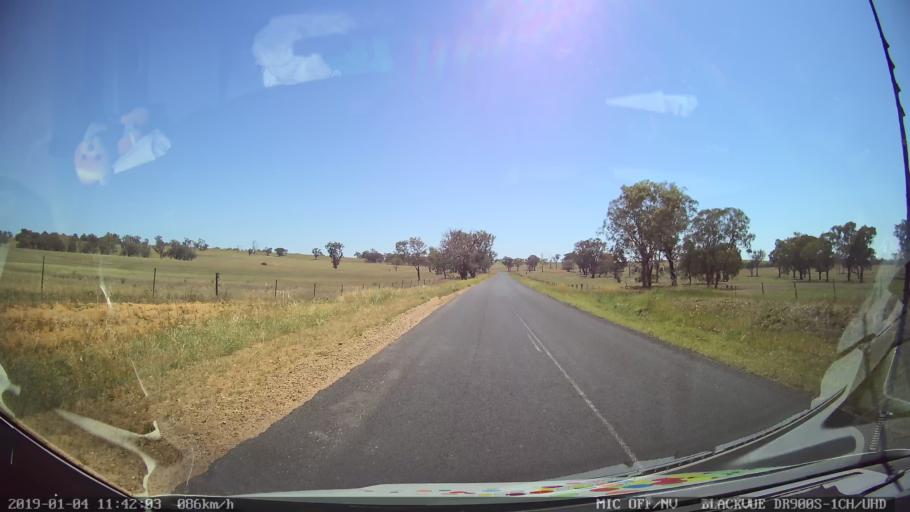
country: AU
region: New South Wales
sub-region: Cabonne
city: Molong
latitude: -32.9863
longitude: 148.7865
